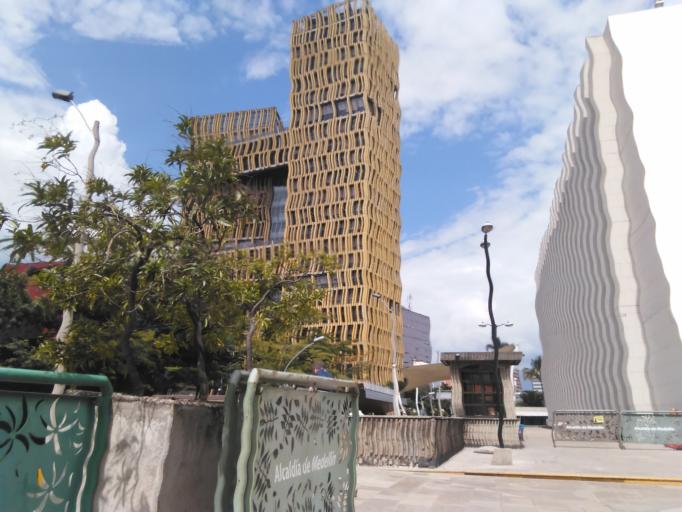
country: CO
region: Antioquia
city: Medellin
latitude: 6.2440
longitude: -75.5743
